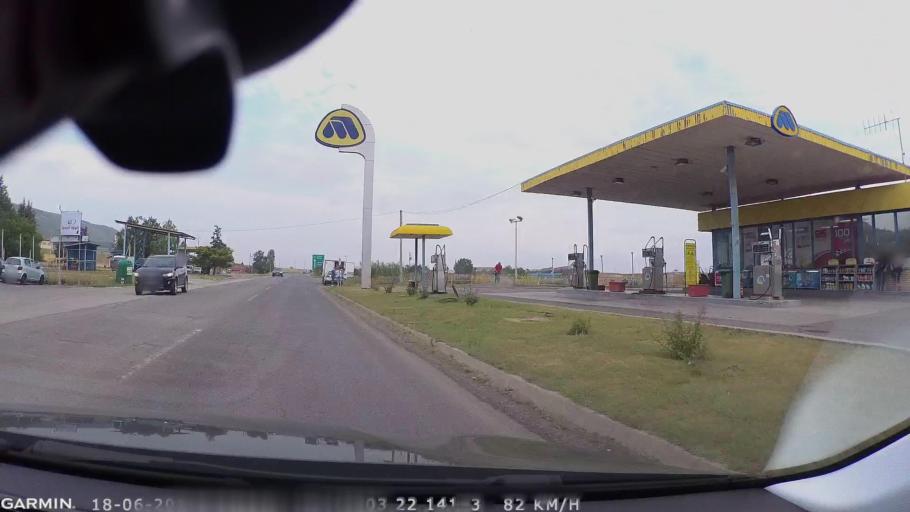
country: MK
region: Stip
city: Shtip
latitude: 41.7736
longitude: 22.1400
